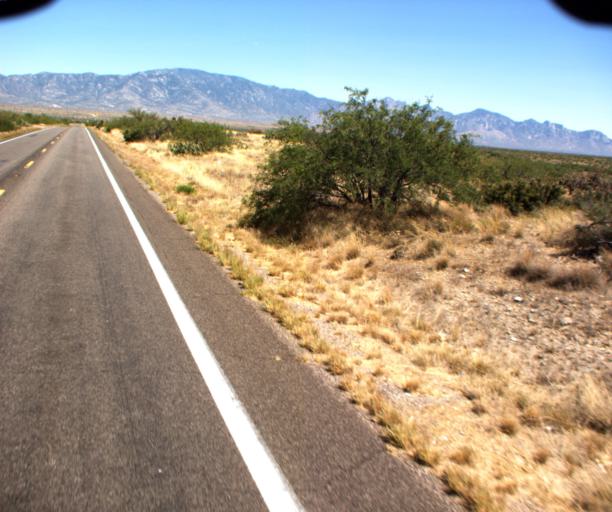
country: US
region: Arizona
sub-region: Pima County
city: Catalina
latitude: 32.5856
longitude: -110.9604
